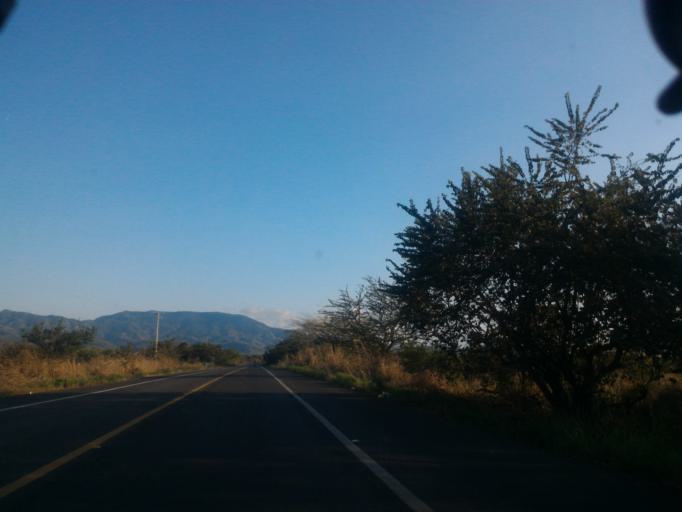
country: MX
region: Michoacan
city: Coahuayana Viejo
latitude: 18.6889
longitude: -103.6979
